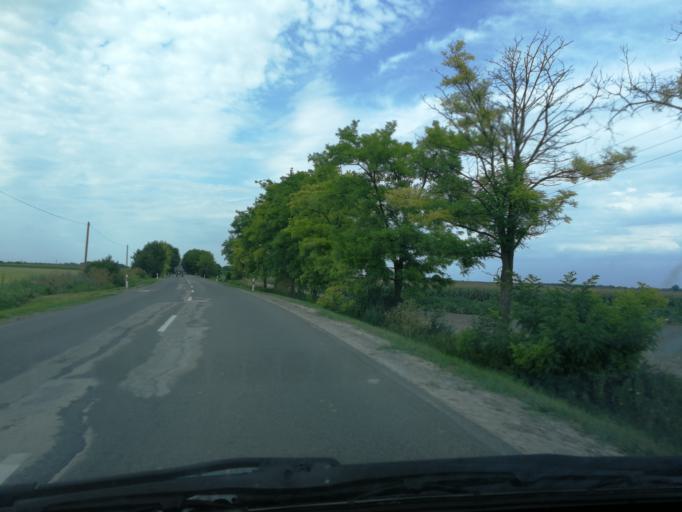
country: HU
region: Bacs-Kiskun
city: Batya
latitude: 46.4475
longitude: 18.9537
